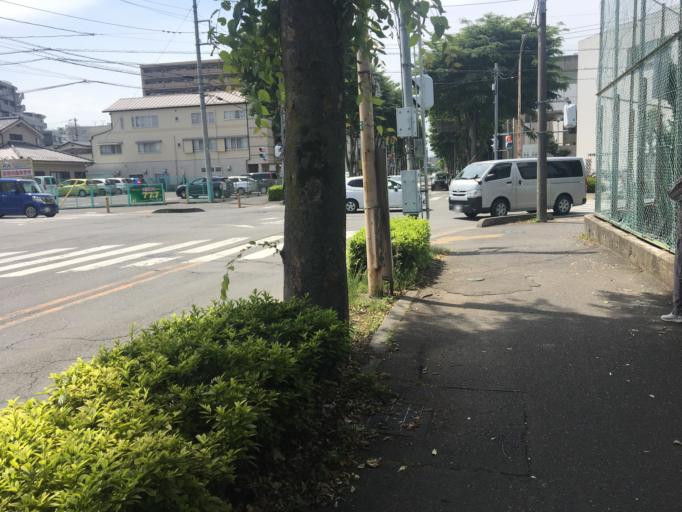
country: JP
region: Saitama
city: Sayama
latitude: 35.8349
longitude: 139.3966
